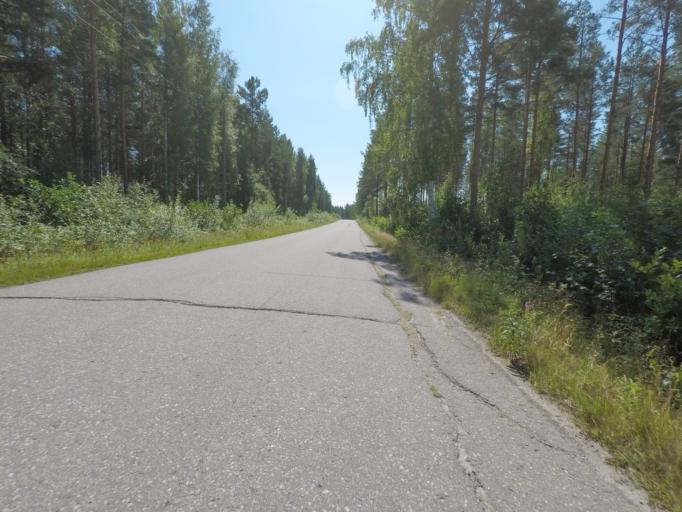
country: FI
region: Southern Savonia
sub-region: Mikkeli
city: Puumala
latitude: 61.4415
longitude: 28.1650
